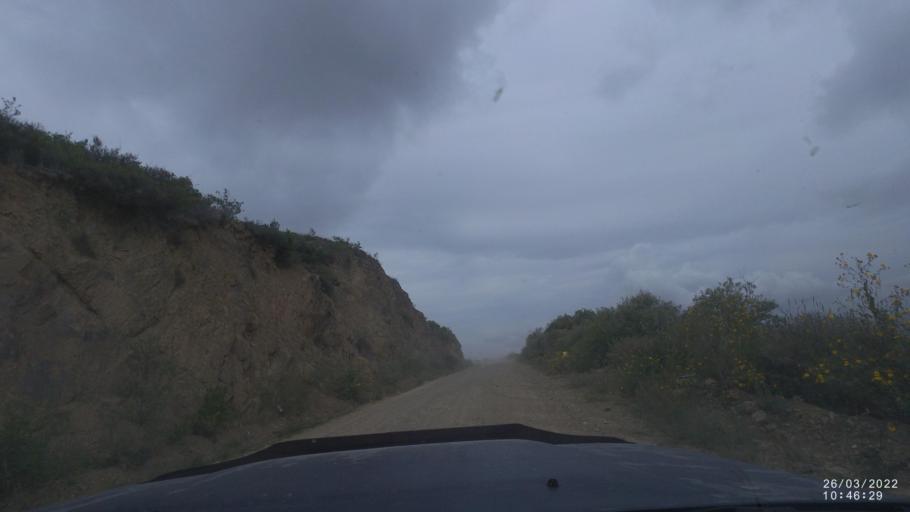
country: BO
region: Cochabamba
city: Tarata
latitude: -17.4871
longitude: -66.0483
